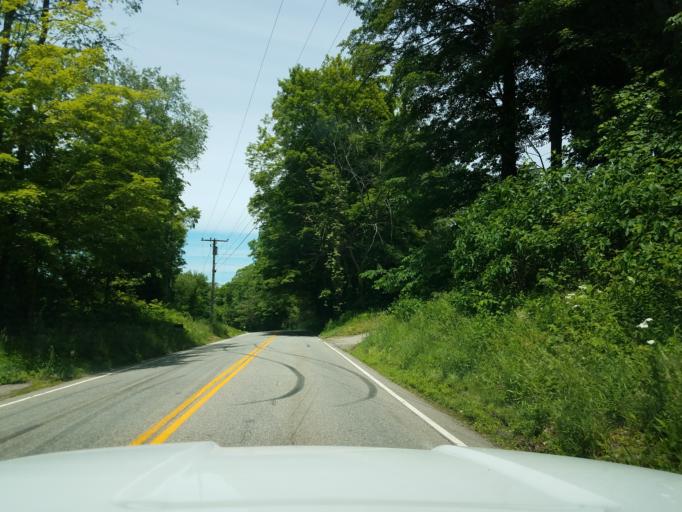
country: US
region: Connecticut
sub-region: Windham County
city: Willimantic
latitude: 41.6555
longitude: -72.2464
